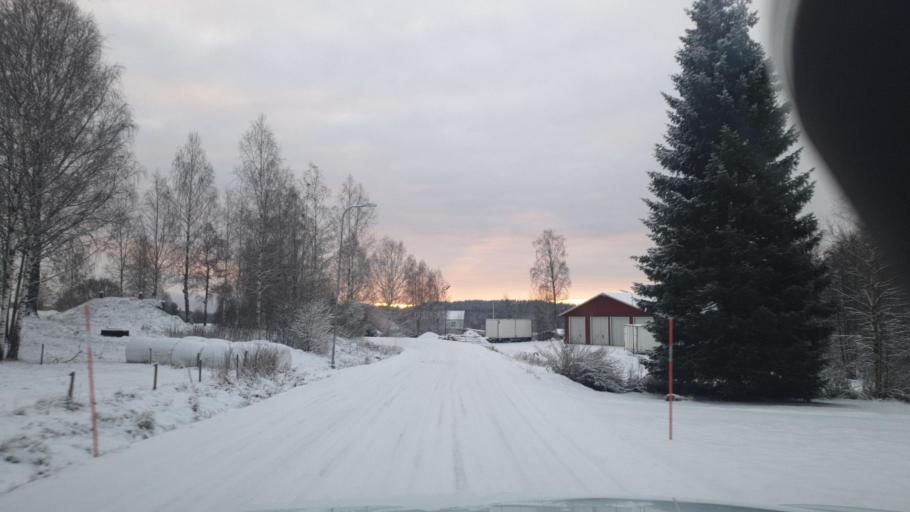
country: NO
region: Hedmark
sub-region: Eidskog
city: Skotterud
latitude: 59.8194
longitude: 12.1475
